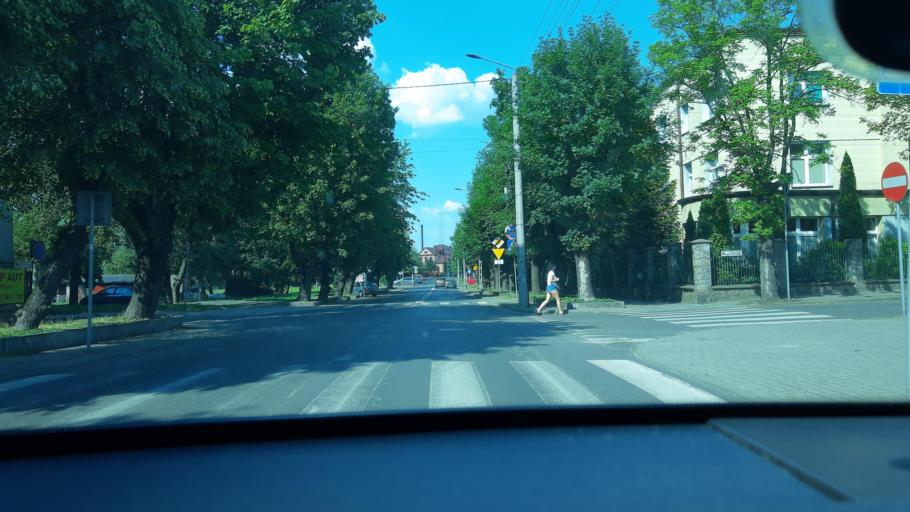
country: PL
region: Lodz Voivodeship
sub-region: Powiat zdunskowolski
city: Zdunska Wola
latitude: 51.6044
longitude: 18.9403
